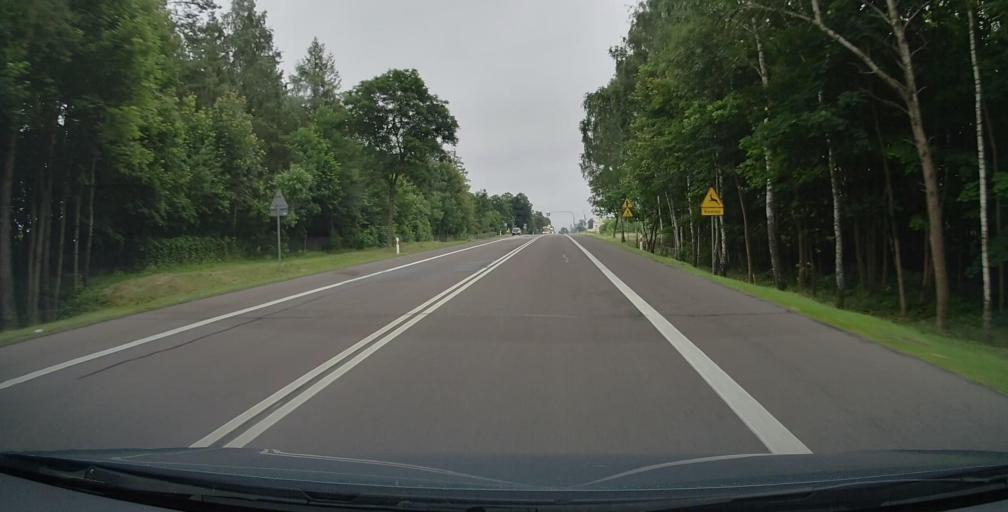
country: PL
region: Lublin Voivodeship
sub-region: Powiat bialski
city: Lesna Podlaska
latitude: 52.0363
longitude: 23.0015
